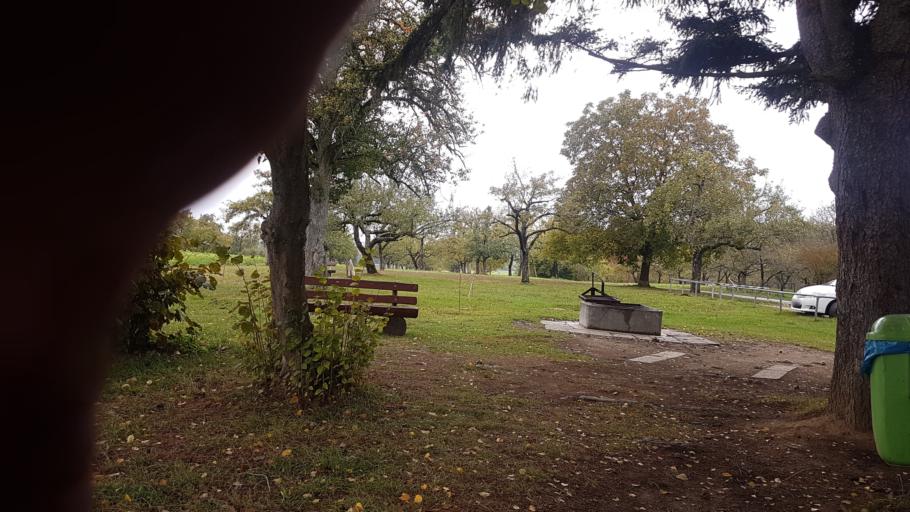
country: DE
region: Baden-Wuerttemberg
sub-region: Tuebingen Region
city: Dusslingen
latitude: 48.4570
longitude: 9.0365
